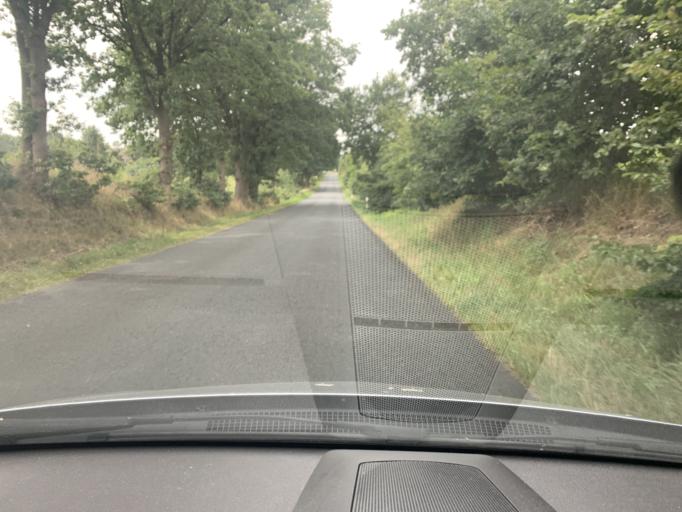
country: DE
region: Schleswig-Holstein
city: Gottin
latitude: 53.5339
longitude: 10.7075
